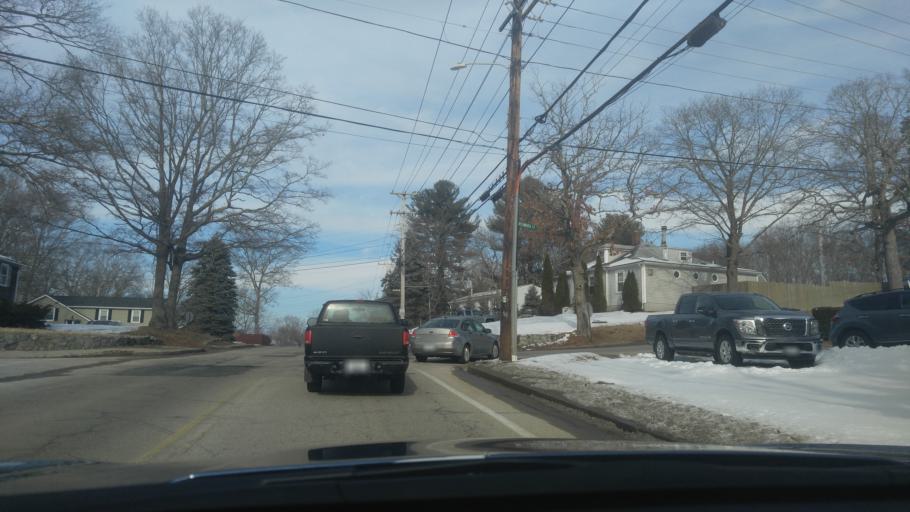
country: US
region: Rhode Island
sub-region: Kent County
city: West Warwick
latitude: 41.6718
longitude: -71.5324
